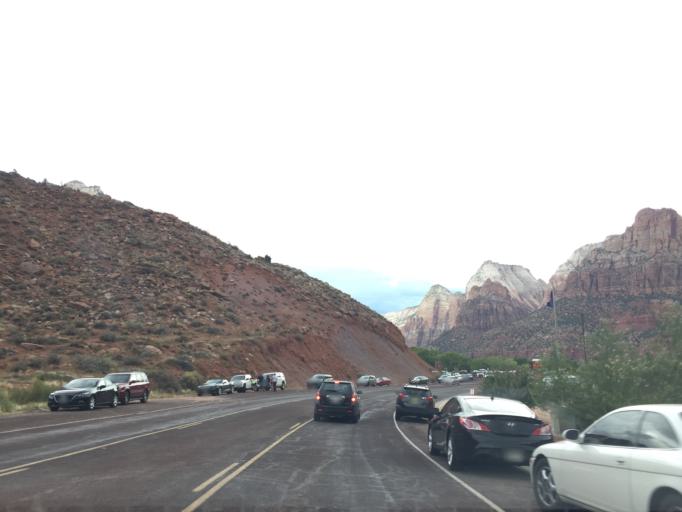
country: US
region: Utah
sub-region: Washington County
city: Hildale
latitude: 37.1996
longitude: -112.9904
